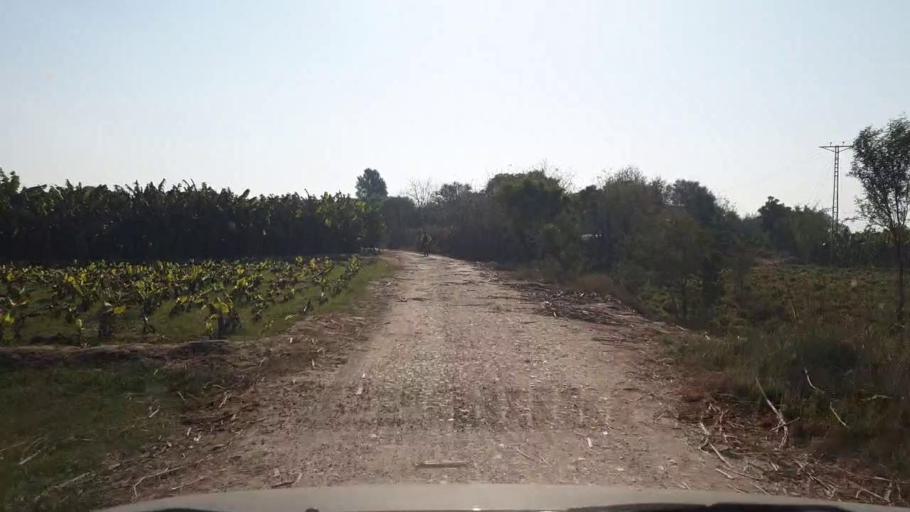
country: PK
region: Sindh
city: Tando Jam
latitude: 25.4272
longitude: 68.6090
